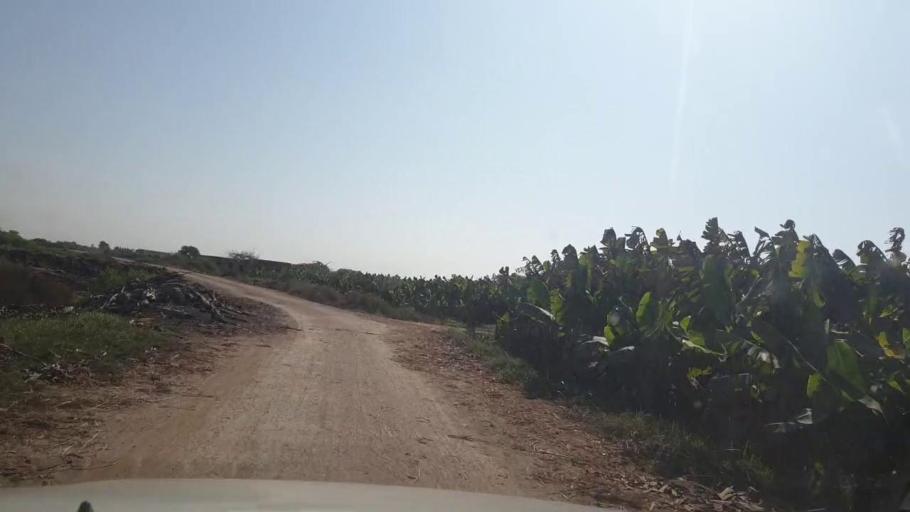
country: PK
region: Sindh
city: Chuhar Jamali
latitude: 24.4502
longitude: 67.8646
